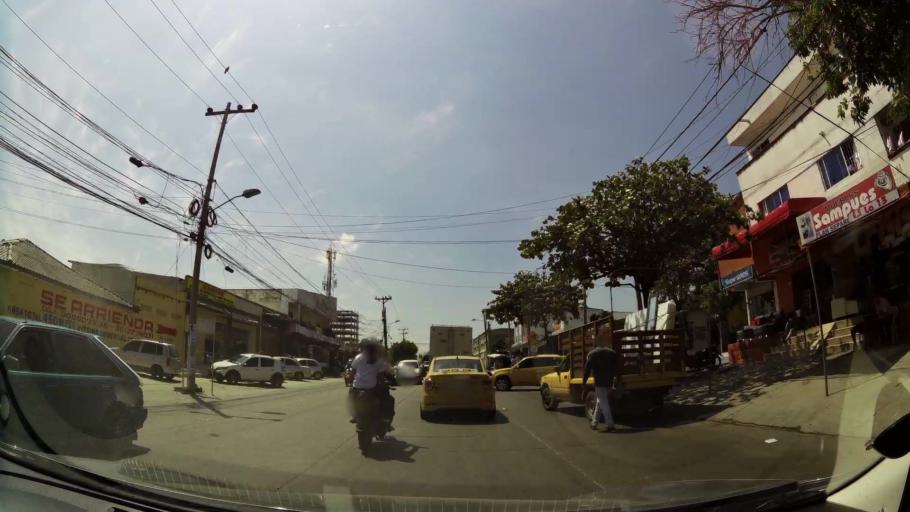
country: CO
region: Atlantico
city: Barranquilla
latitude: 10.9581
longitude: -74.8042
